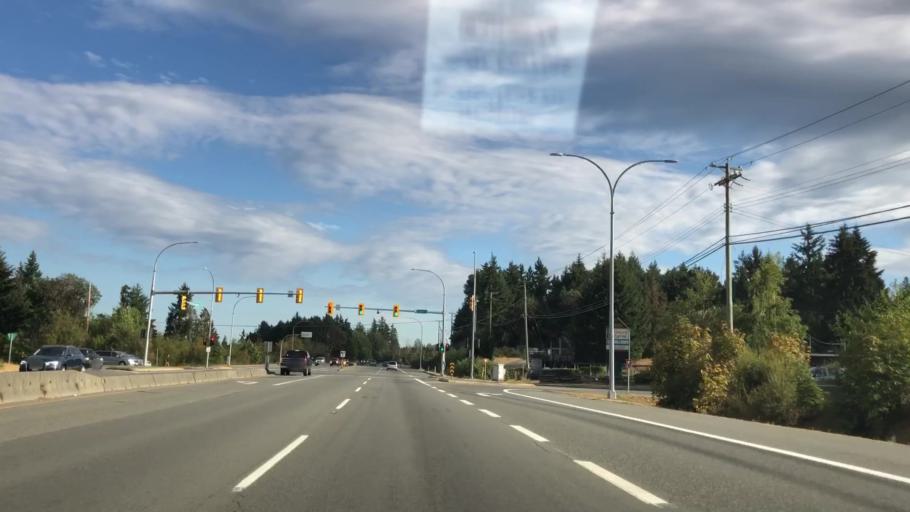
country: CA
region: British Columbia
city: North Saanich
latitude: 48.6427
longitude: -123.5545
